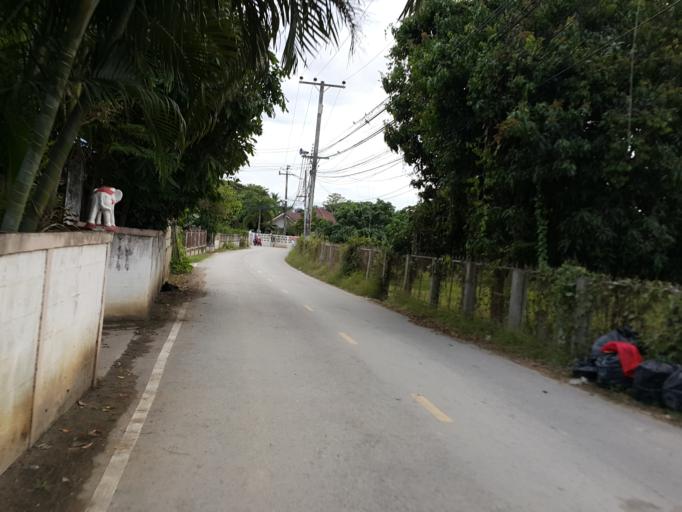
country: TH
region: Chiang Mai
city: San Sai
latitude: 18.8685
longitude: 99.1125
